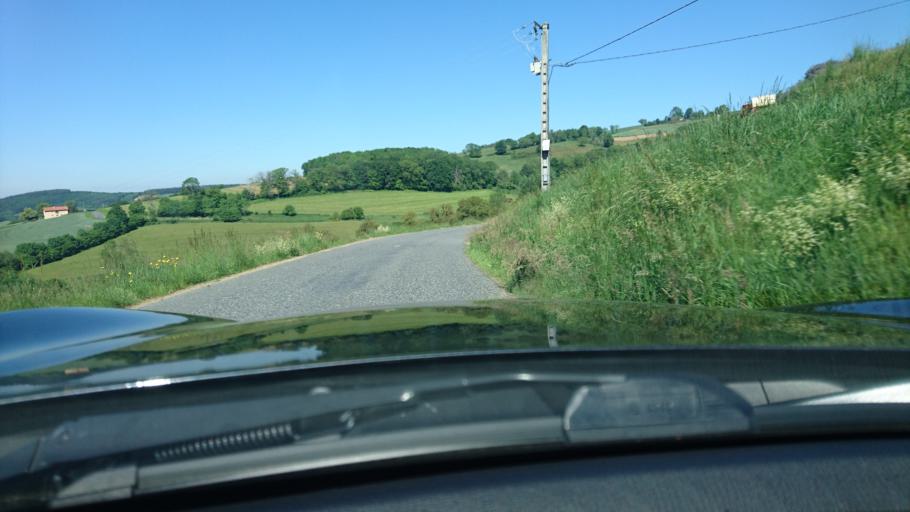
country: FR
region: Rhone-Alpes
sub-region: Departement de la Loire
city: Violay
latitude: 45.8282
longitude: 4.3866
